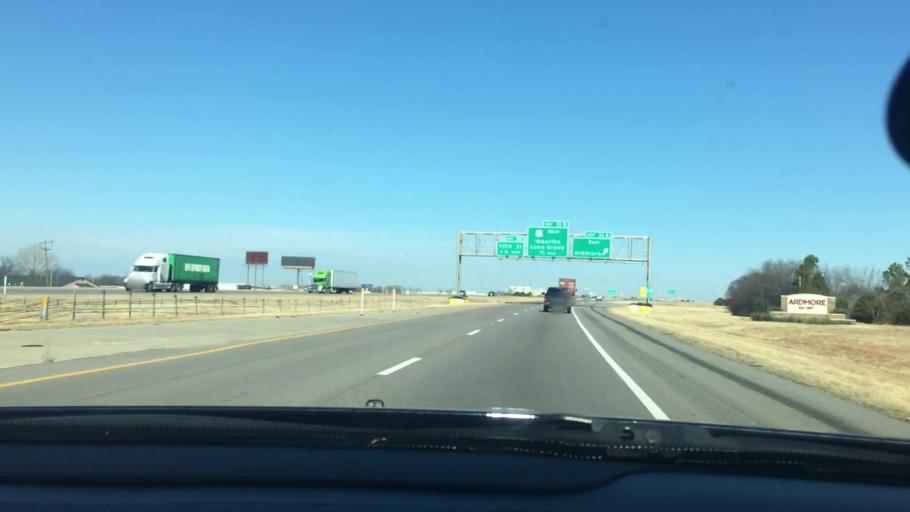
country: US
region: Oklahoma
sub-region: Carter County
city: Ardmore
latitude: 34.1667
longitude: -97.1671
